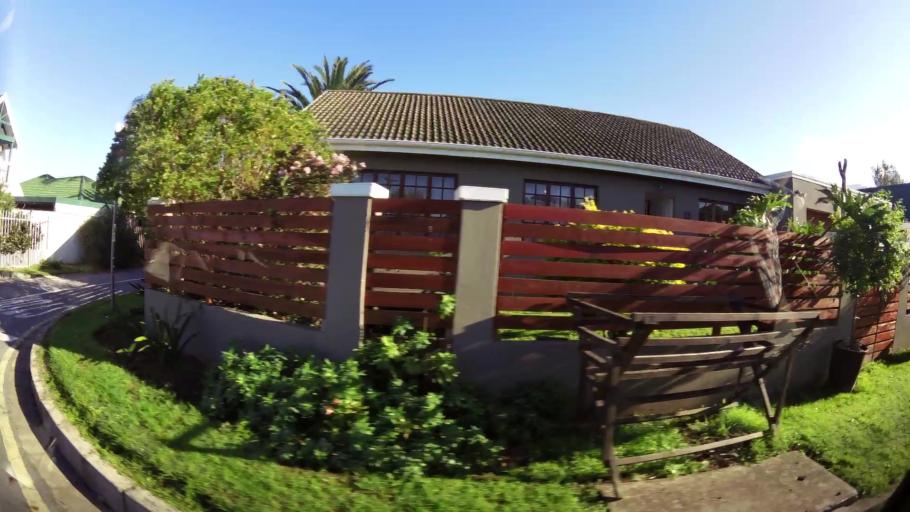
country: ZA
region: Western Cape
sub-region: Eden District Municipality
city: George
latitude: -33.9616
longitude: 22.4448
